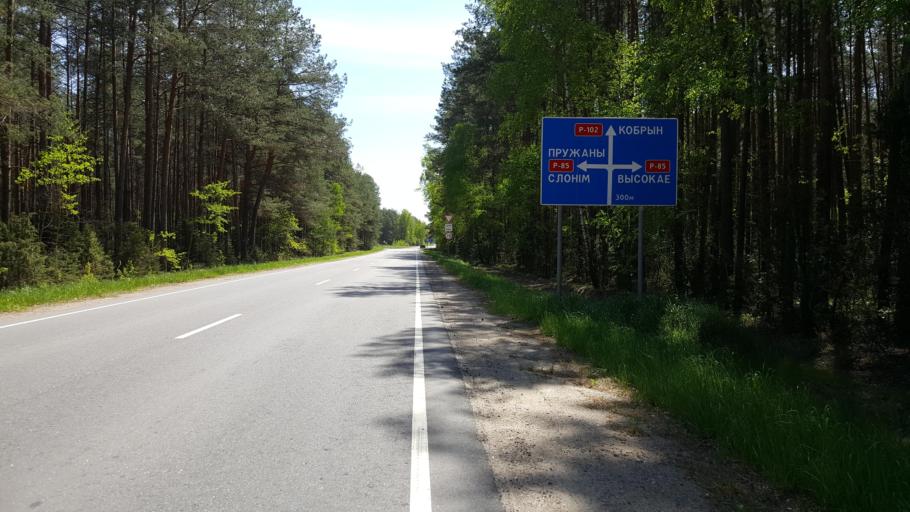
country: BY
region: Brest
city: Zhabinka
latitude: 52.3816
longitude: 24.1186
